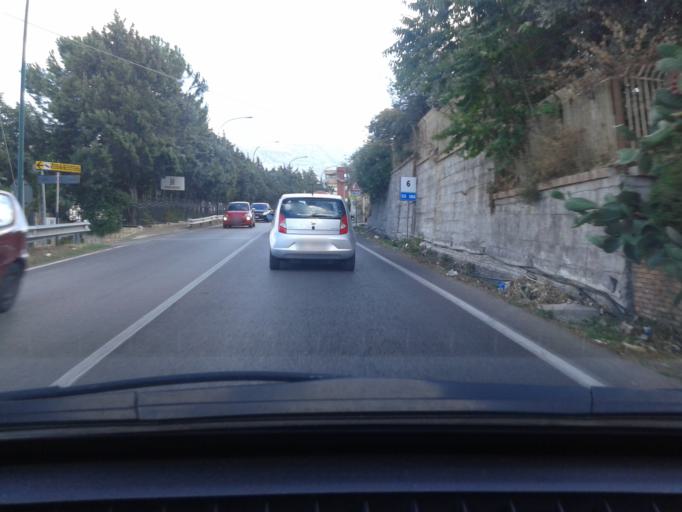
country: IT
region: Sicily
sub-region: Palermo
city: Monreale
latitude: 38.0818
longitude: 13.2994
